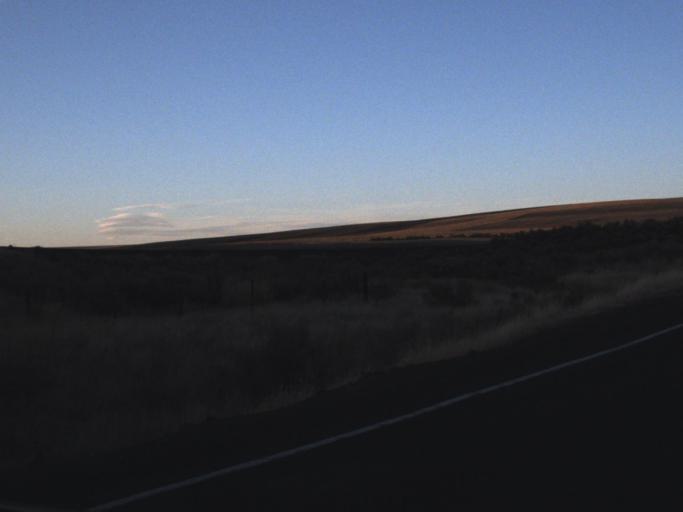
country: US
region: Washington
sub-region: Adams County
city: Ritzville
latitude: 46.9732
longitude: -118.6642
